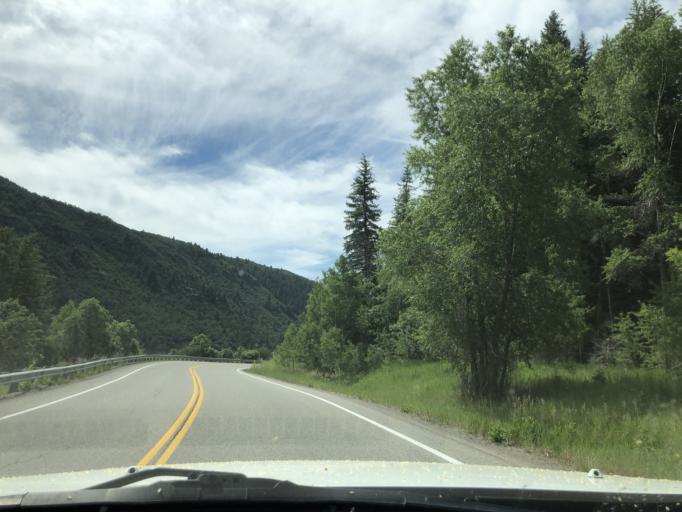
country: US
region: Colorado
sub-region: Delta County
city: Paonia
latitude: 38.9728
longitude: -107.3415
